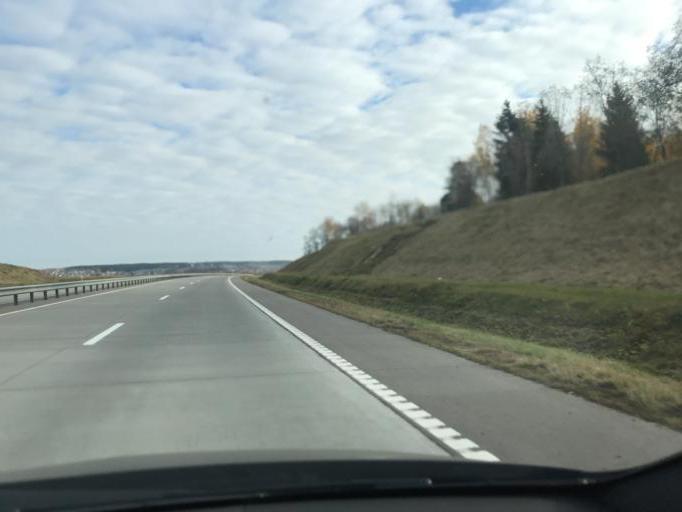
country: BY
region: Minsk
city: Pyatryshki
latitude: 54.0528
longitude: 27.1928
